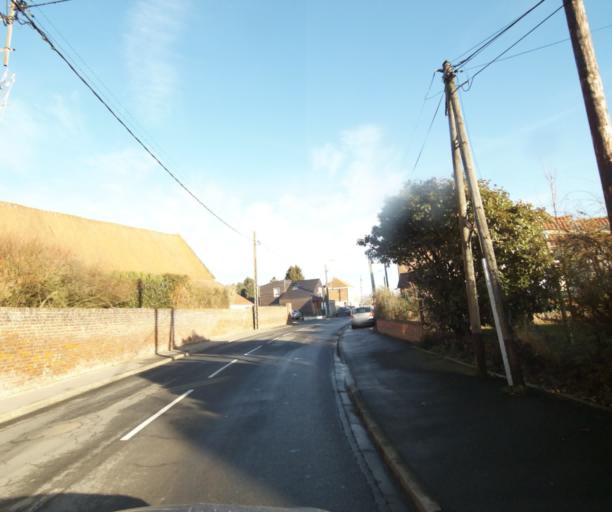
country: FR
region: Nord-Pas-de-Calais
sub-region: Departement du Nord
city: Saultain
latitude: 50.3412
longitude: 3.5789
